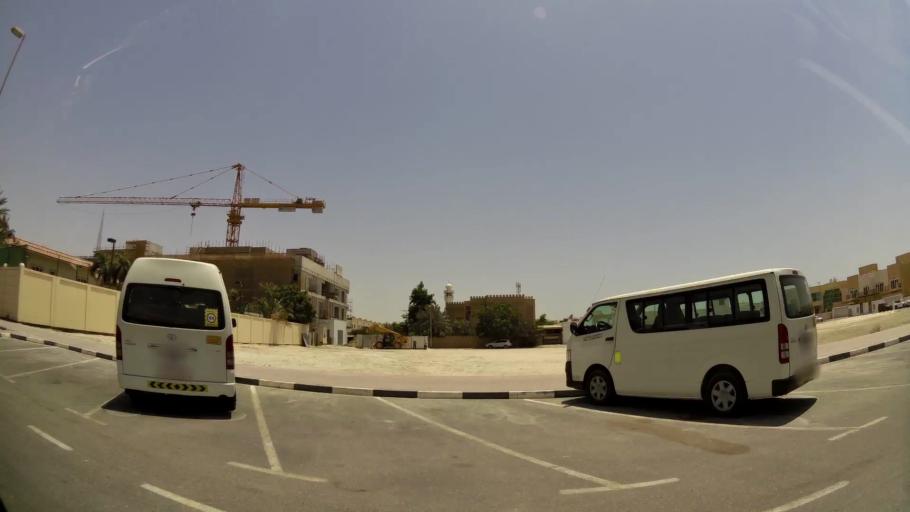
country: AE
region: Dubai
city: Dubai
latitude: 25.2250
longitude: 55.2643
